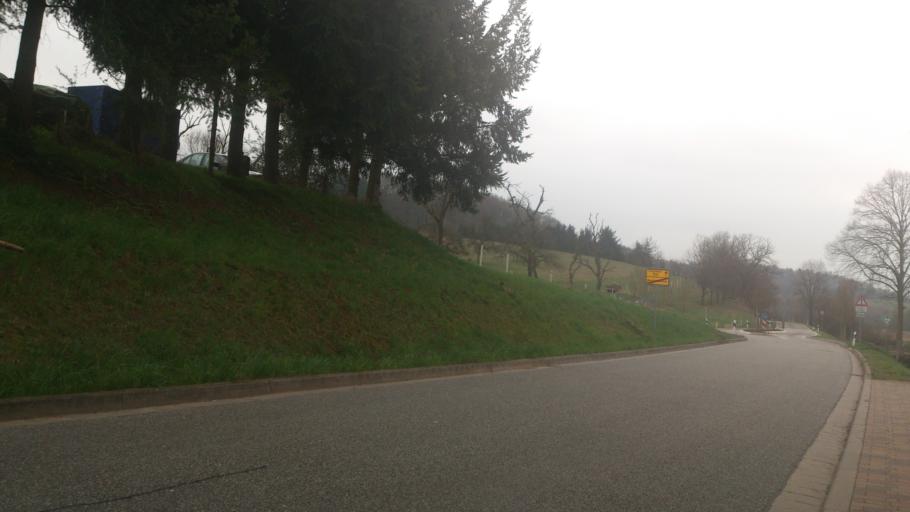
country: DE
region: Rheinland-Pfalz
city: Nanzdietschweiler
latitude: 49.4384
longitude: 7.4394
